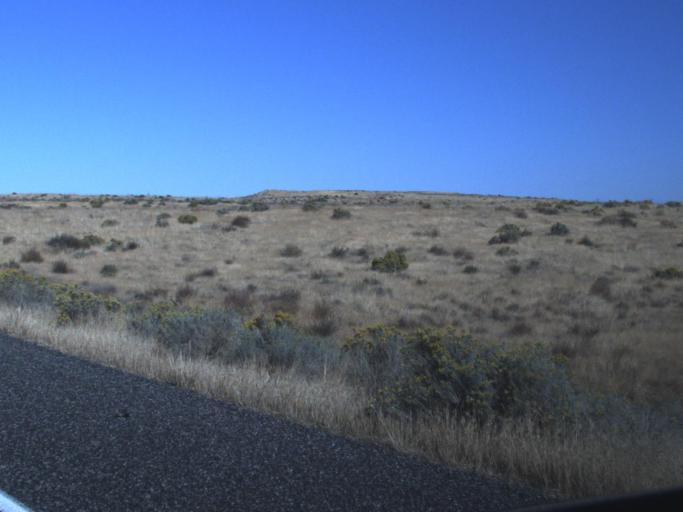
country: US
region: Washington
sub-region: Benton County
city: West Richland
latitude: 46.3819
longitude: -119.4202
